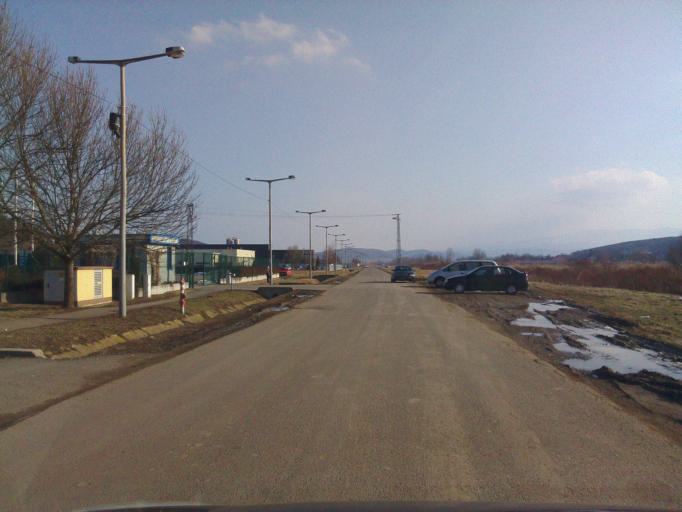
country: HU
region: Nograd
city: Salgotarjan
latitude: 48.0439
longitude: 19.7952
